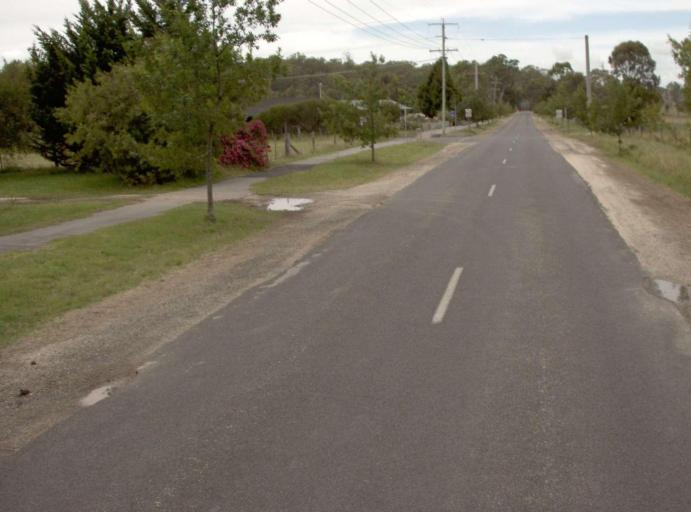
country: AU
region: Victoria
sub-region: Wellington
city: Sale
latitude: -37.8455
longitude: 147.0722
